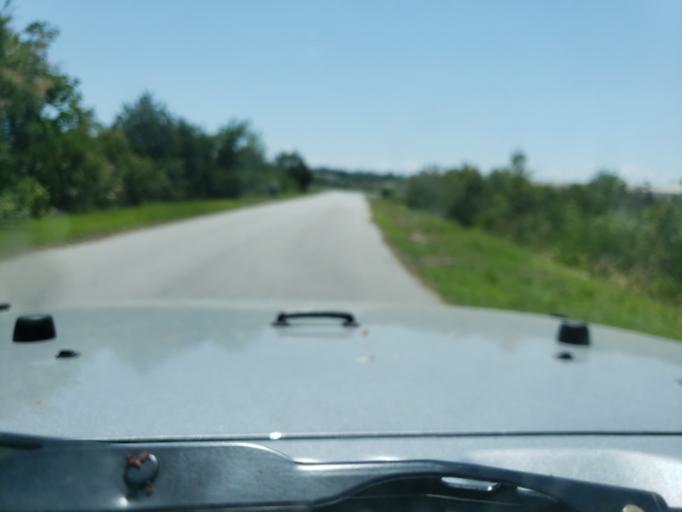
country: US
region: Georgia
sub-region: Chatham County
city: Thunderbolt
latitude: 32.0743
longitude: -81.0448
